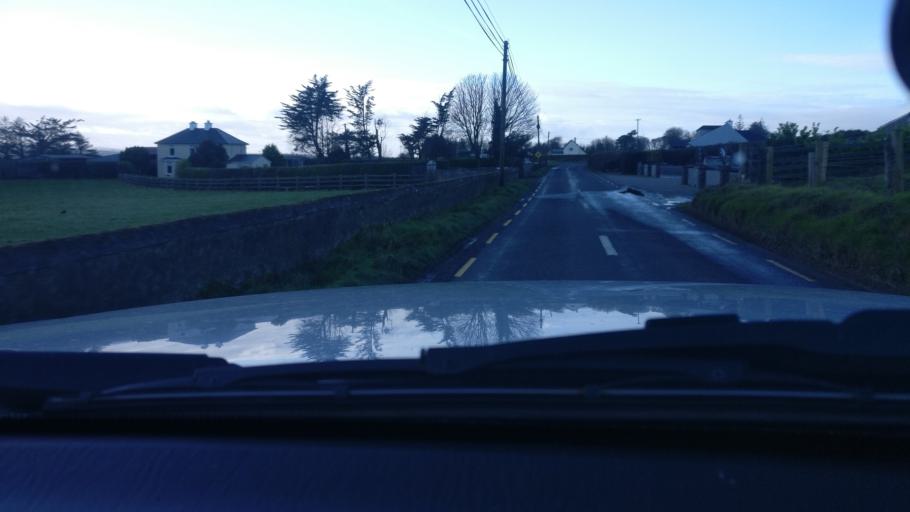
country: IE
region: Connaught
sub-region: County Galway
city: Loughrea
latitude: 53.2272
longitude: -8.4238
